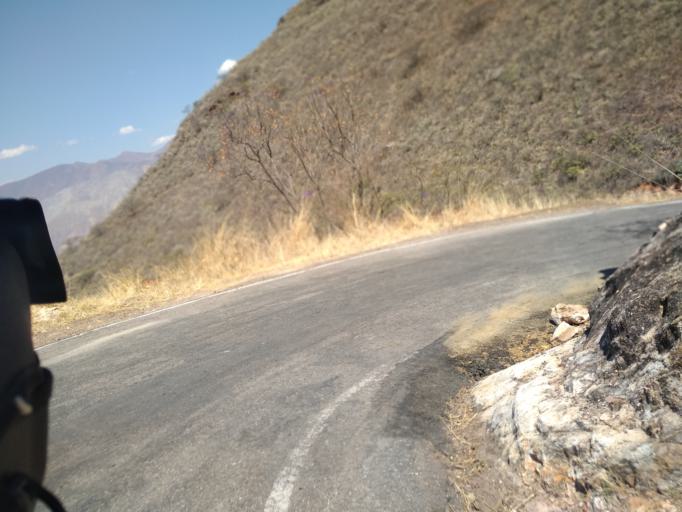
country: PE
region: Amazonas
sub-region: Provincia de Chachapoyas
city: Balsas
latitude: -6.8496
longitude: -77.9783
